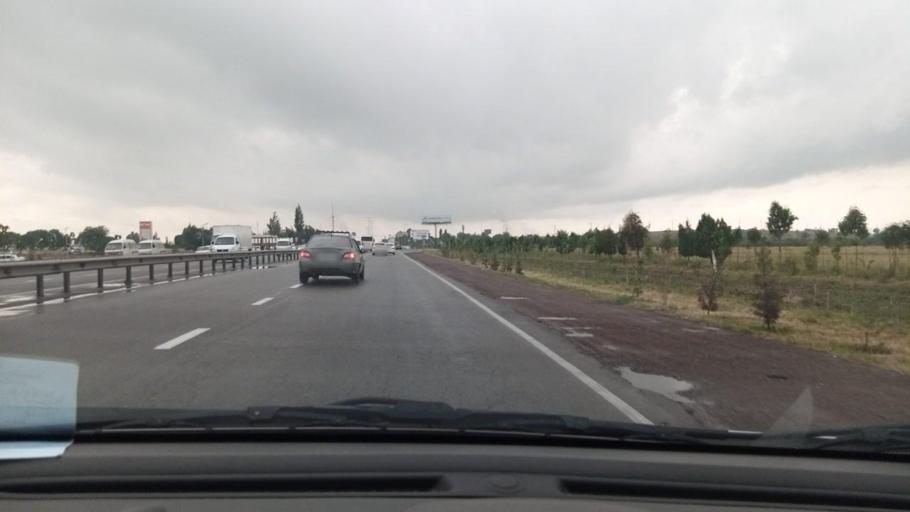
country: UZ
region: Toshkent
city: Ohangaron
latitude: 40.9185
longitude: 69.6013
